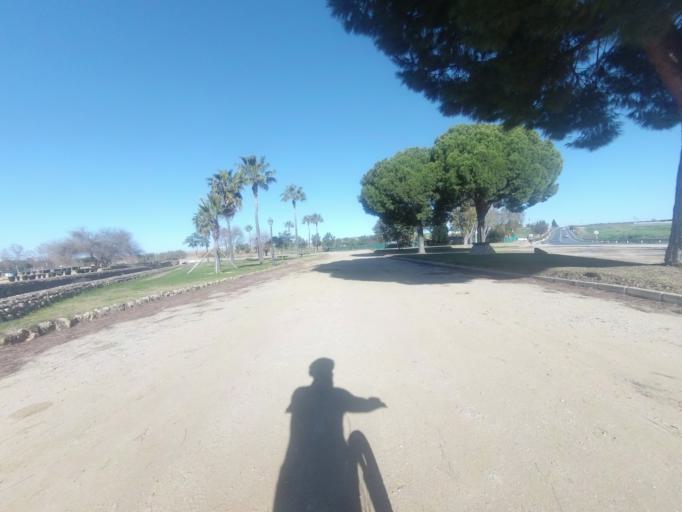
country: ES
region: Andalusia
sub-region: Provincia de Huelva
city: Palos de la Frontera
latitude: 37.2321
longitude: -6.8903
